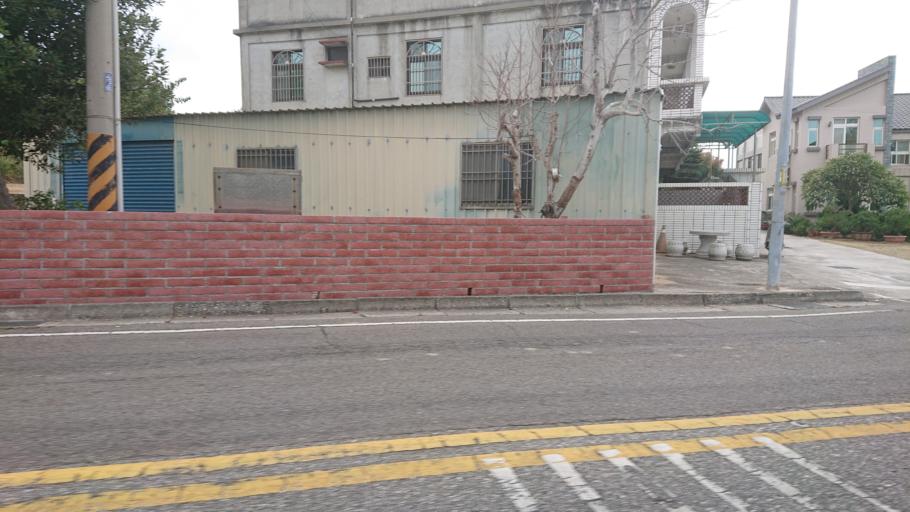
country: TW
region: Fukien
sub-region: Kinmen
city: Jincheng
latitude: 24.4208
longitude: 118.3173
